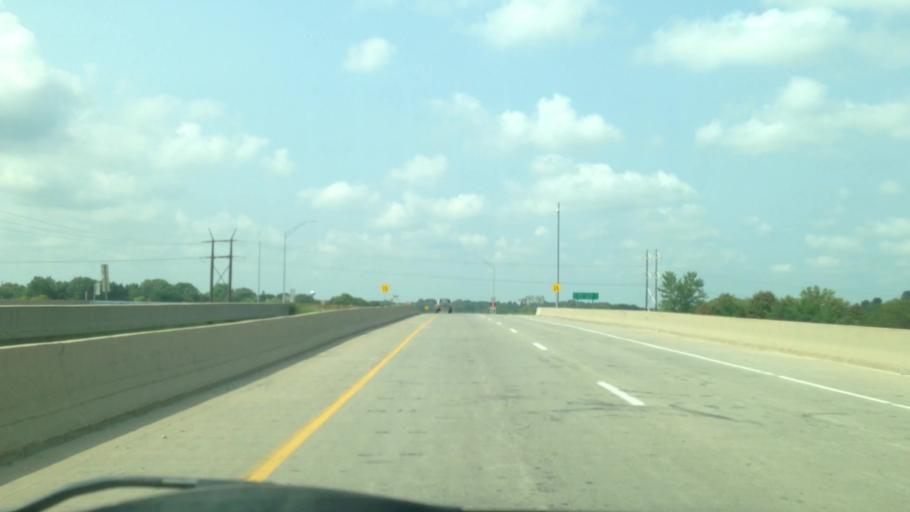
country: US
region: Iowa
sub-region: Linn County
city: Fairfax
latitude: 41.9455
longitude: -91.7407
